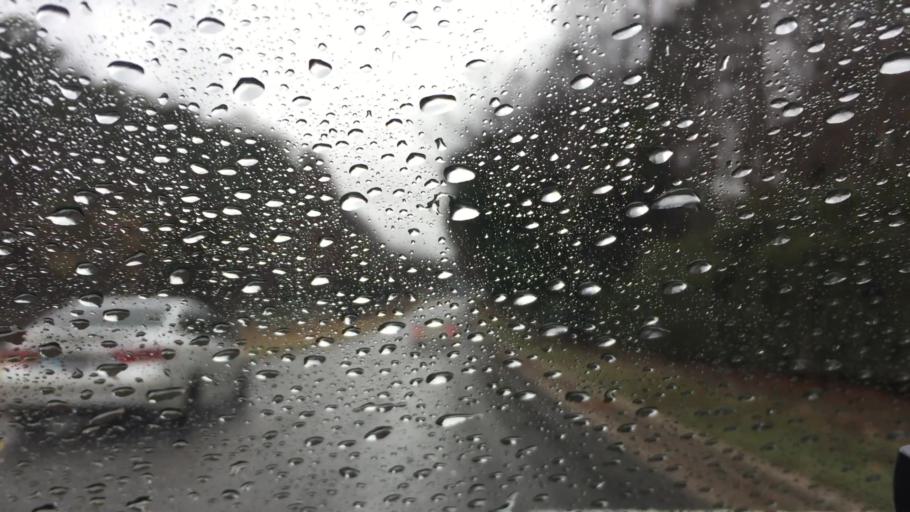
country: US
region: North Carolina
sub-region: Wake County
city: Cary
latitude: 35.7551
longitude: -78.8021
